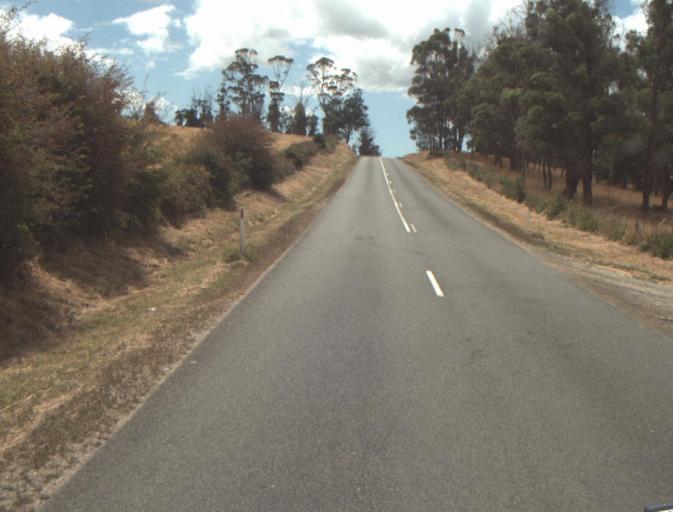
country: AU
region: Tasmania
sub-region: Launceston
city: Mayfield
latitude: -41.2218
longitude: 147.1216
